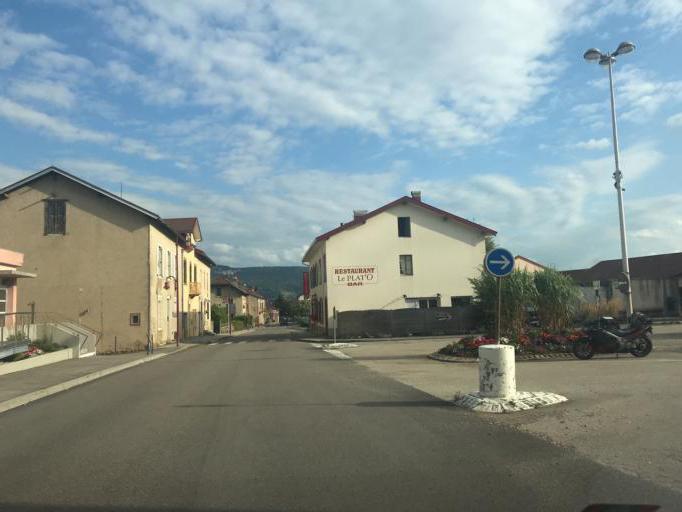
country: FR
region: Franche-Comte
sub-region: Departement du Jura
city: Saint-Lupicin
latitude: 46.3982
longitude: 5.7936
